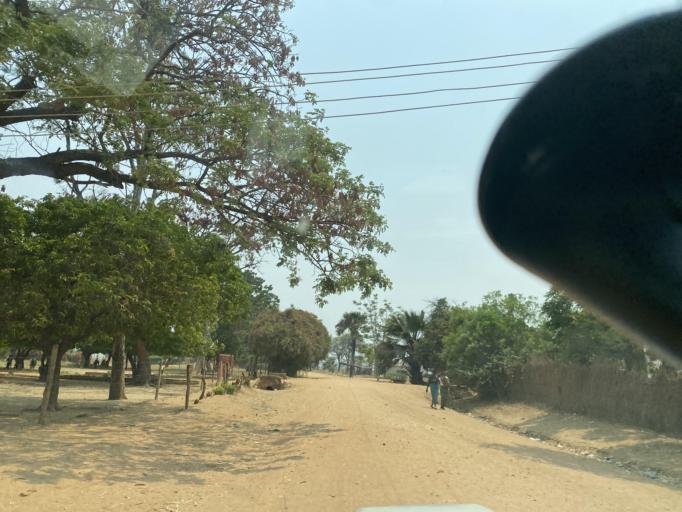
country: ZM
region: Lusaka
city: Kafue
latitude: -15.6425
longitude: 28.0981
